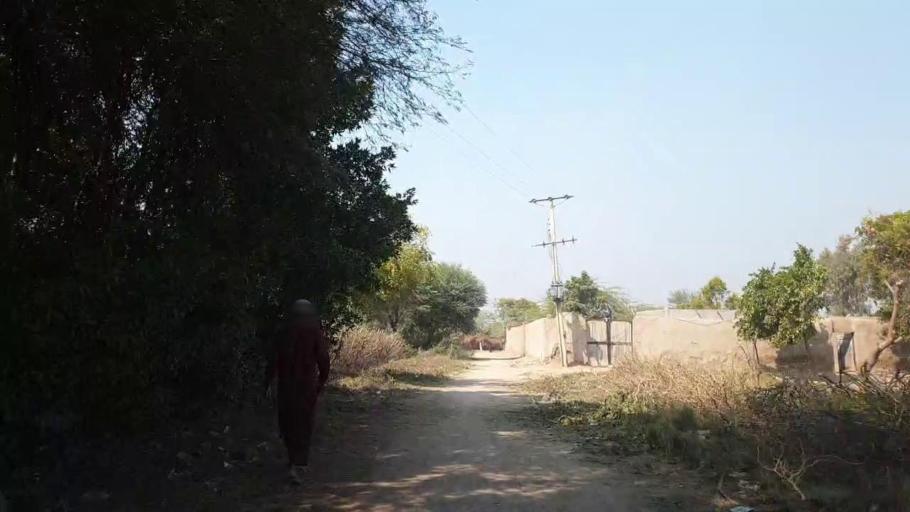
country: PK
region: Sindh
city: Tando Allahyar
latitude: 25.4843
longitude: 68.8006
